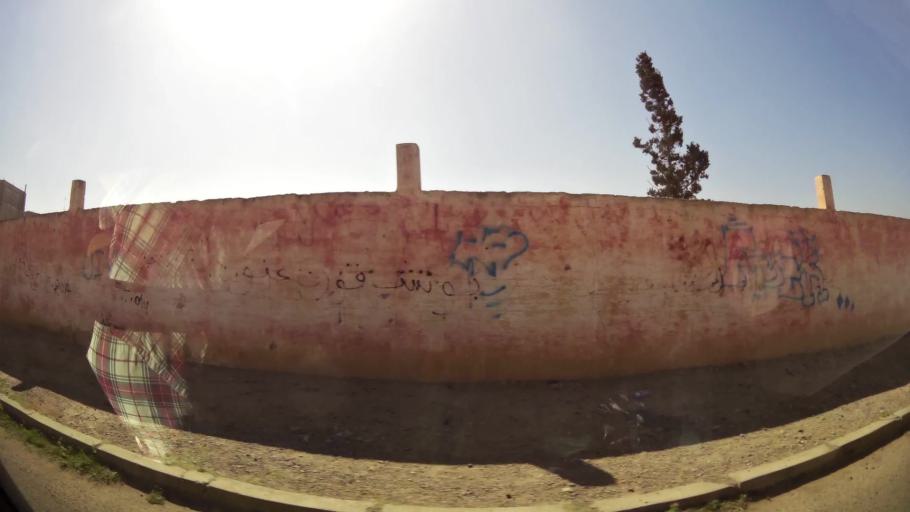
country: MA
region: Souss-Massa-Draa
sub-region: Inezgane-Ait Mellou
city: Inezgane
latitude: 30.3285
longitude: -9.5230
